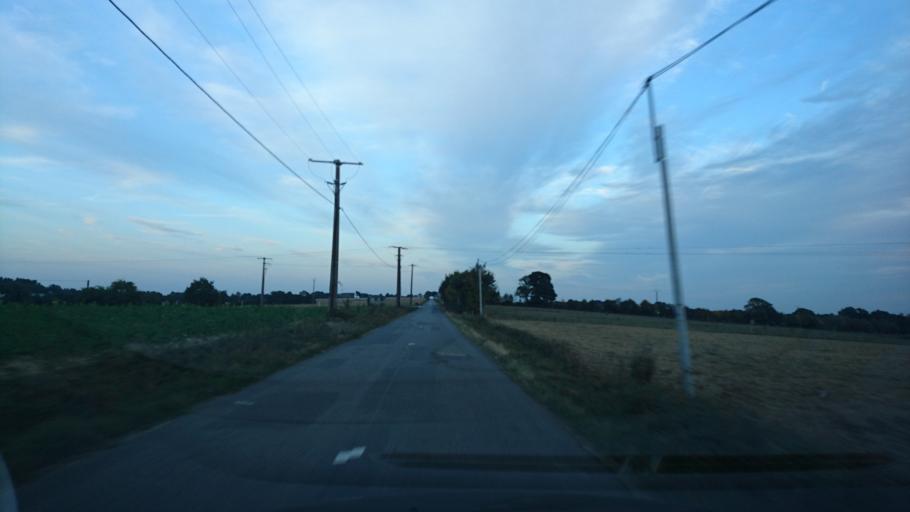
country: FR
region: Brittany
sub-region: Departement d'Ille-et-Vilaine
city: Pipriac
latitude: 47.8183
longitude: -2.0022
